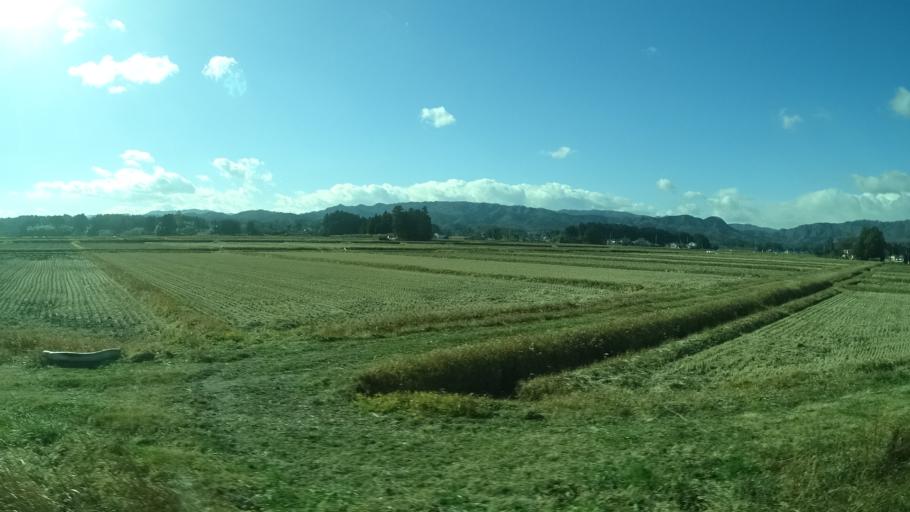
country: JP
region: Miyagi
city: Marumori
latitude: 37.7721
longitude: 140.9204
